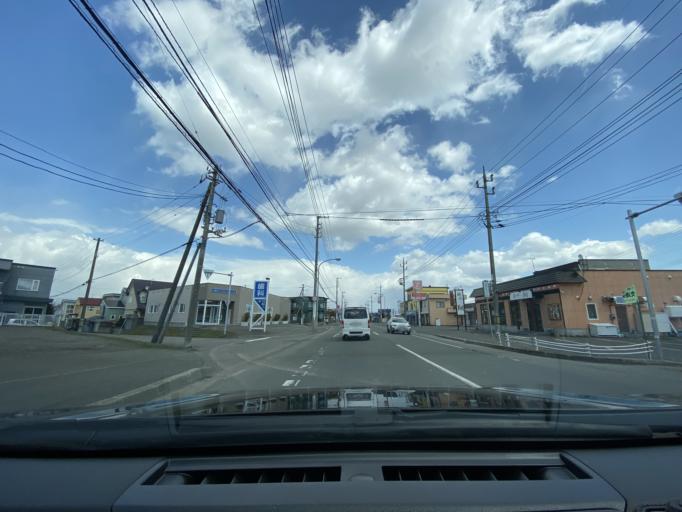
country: JP
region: Hokkaido
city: Kitahiroshima
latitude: 42.9778
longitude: 141.4824
